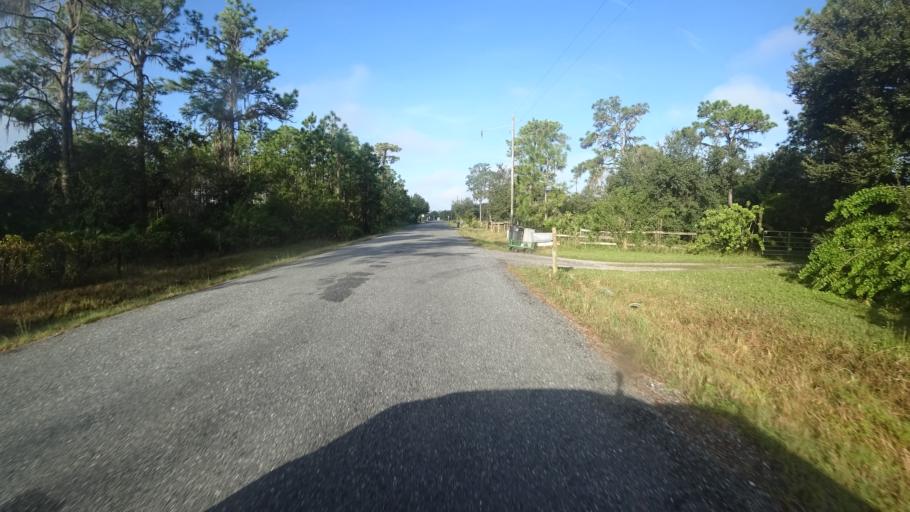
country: US
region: Florida
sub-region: Sarasota County
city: The Meadows
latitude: 27.4054
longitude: -82.3014
